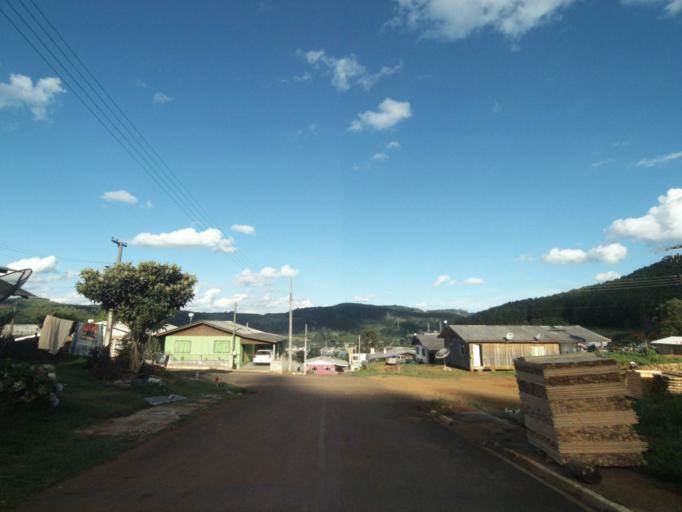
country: BR
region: Parana
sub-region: Uniao Da Vitoria
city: Uniao da Vitoria
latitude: -26.1674
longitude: -51.5384
